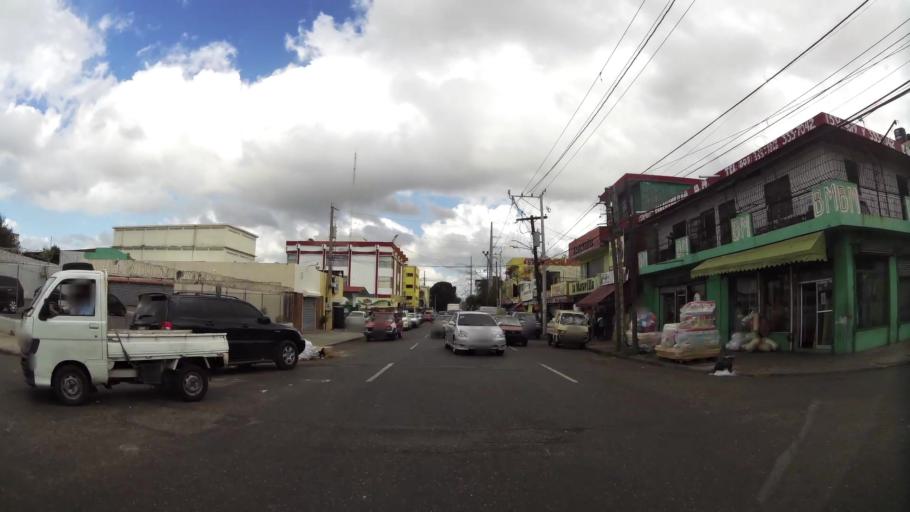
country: DO
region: Nacional
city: San Carlos
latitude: 18.4901
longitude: -69.8968
